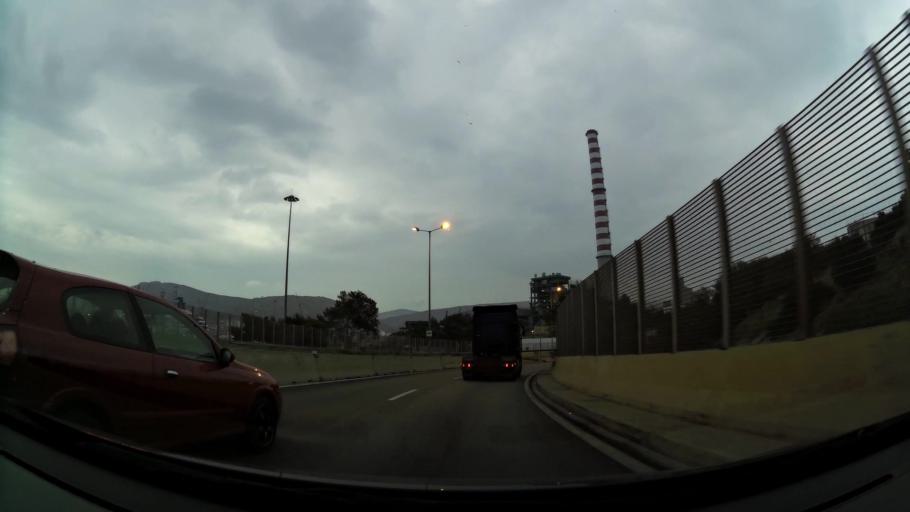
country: GR
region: Attica
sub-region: Nomos Piraios
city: Drapetsona
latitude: 37.9513
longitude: 23.6095
